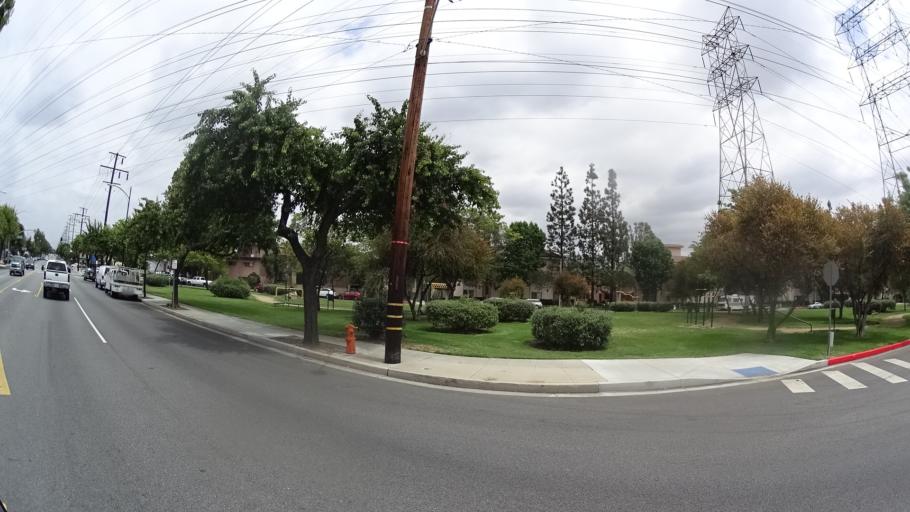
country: US
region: California
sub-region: Los Angeles County
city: Universal City
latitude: 34.1636
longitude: -118.3449
